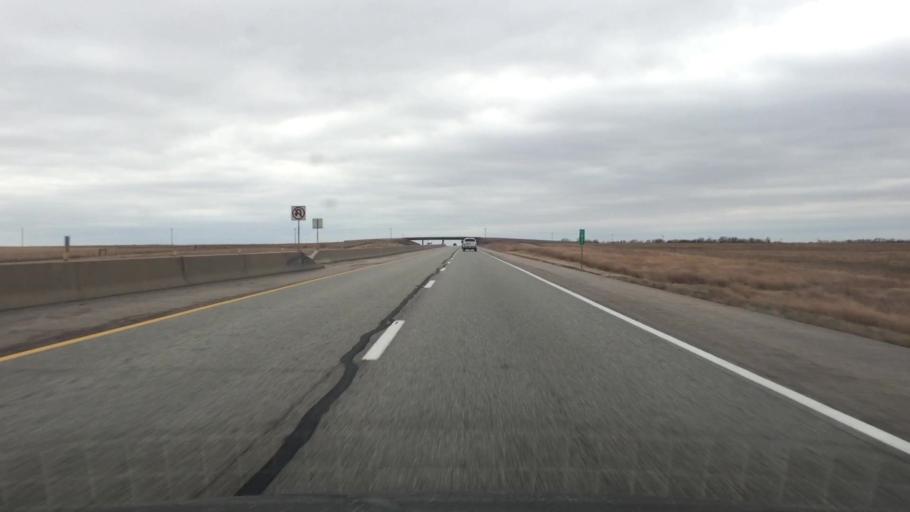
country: US
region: Kansas
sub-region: Butler County
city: El Dorado
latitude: 37.9892
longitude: -96.7027
